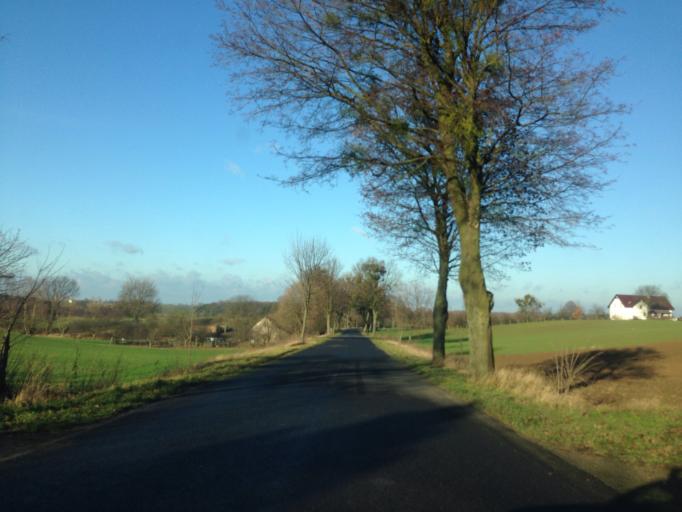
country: PL
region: Kujawsko-Pomorskie
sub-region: Powiat brodnicki
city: Jablonowo Pomorskie
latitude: 53.4110
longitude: 19.1364
